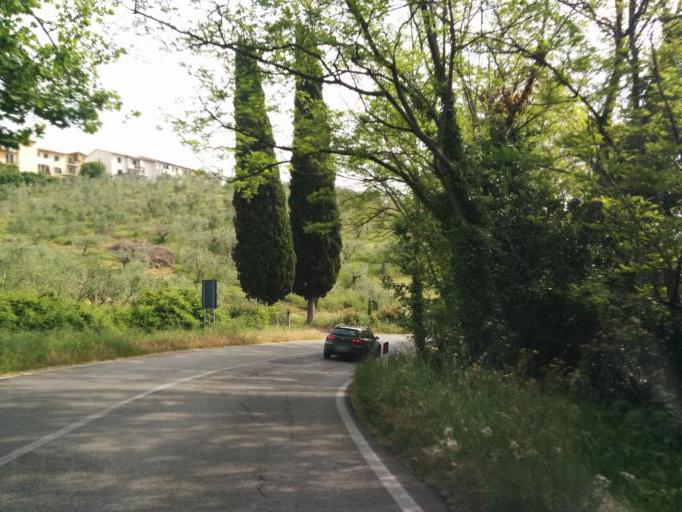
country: IT
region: Tuscany
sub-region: Province of Florence
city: San Casciano in Val di Pesa
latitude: 43.6526
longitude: 11.1891
